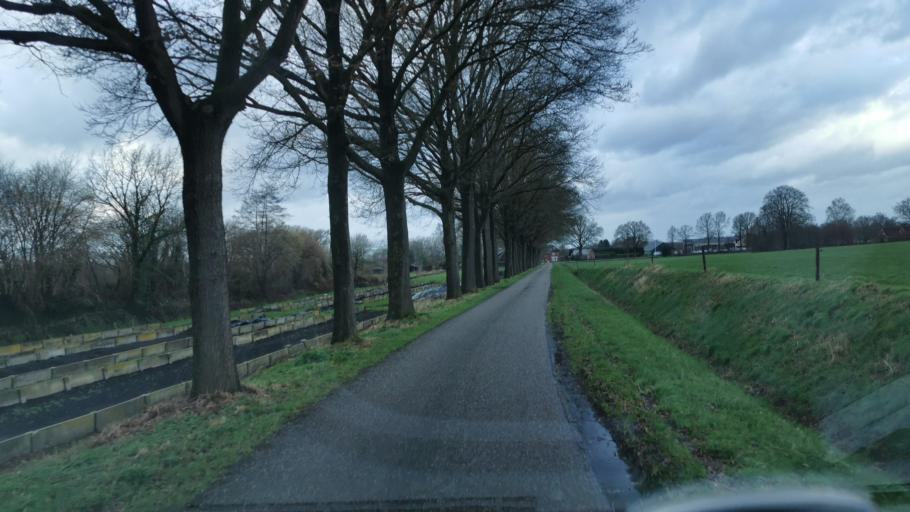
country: DE
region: Lower Saxony
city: Lage
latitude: 52.4204
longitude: 6.9771
